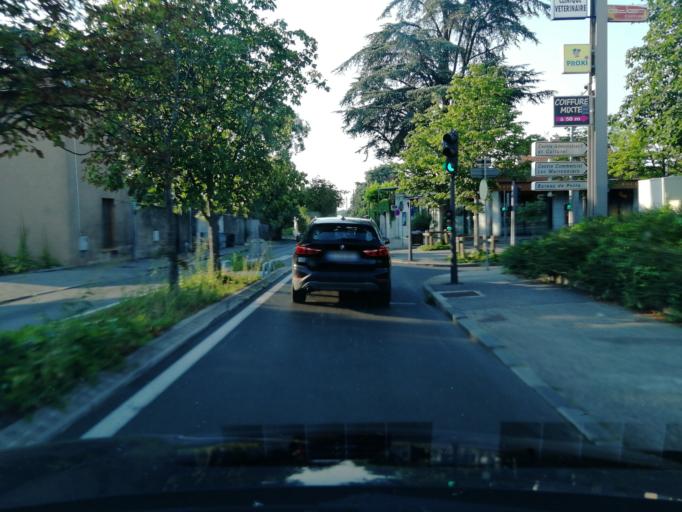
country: FR
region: Rhone-Alpes
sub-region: Departement du Rhone
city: Sathonay-Camp
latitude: 45.8214
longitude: 4.8625
